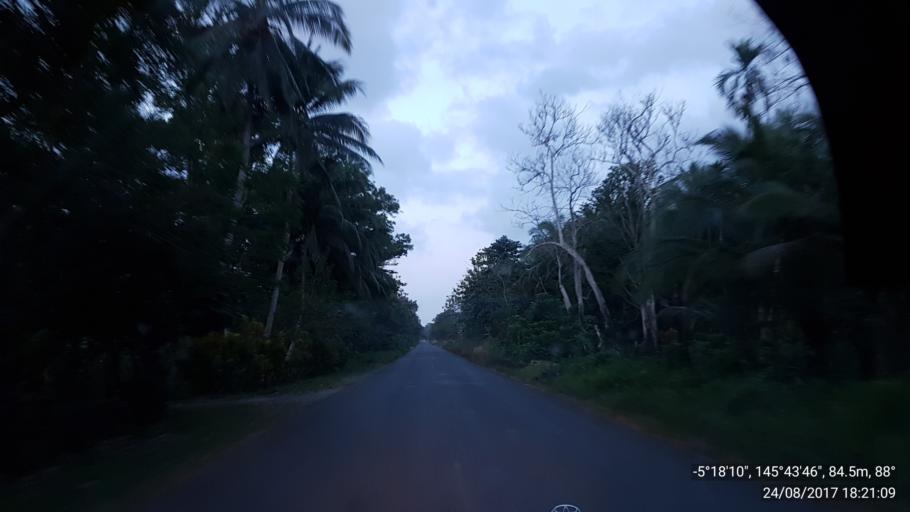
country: PG
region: Madang
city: Madang
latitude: -5.3028
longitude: 145.7297
